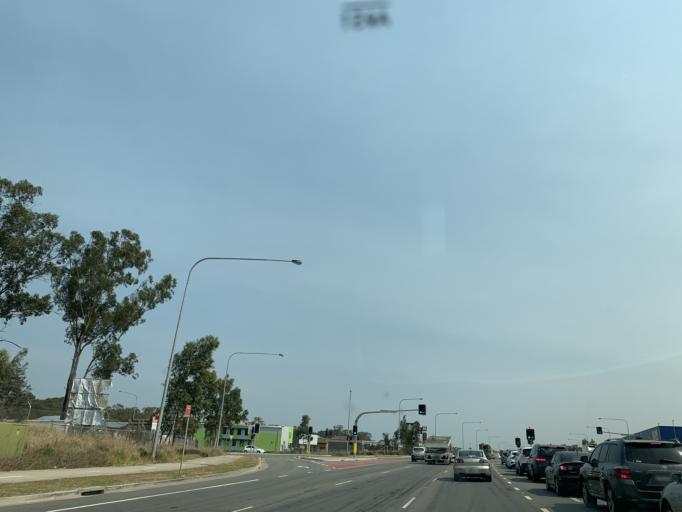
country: AU
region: New South Wales
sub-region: Blacktown
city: Hassall Grove
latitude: -33.7168
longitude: 150.8441
